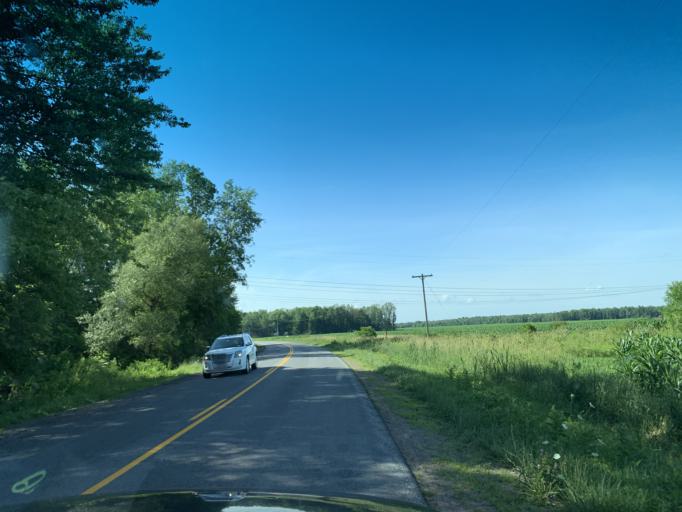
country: US
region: New York
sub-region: Madison County
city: Oneida
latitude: 43.1612
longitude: -75.6722
